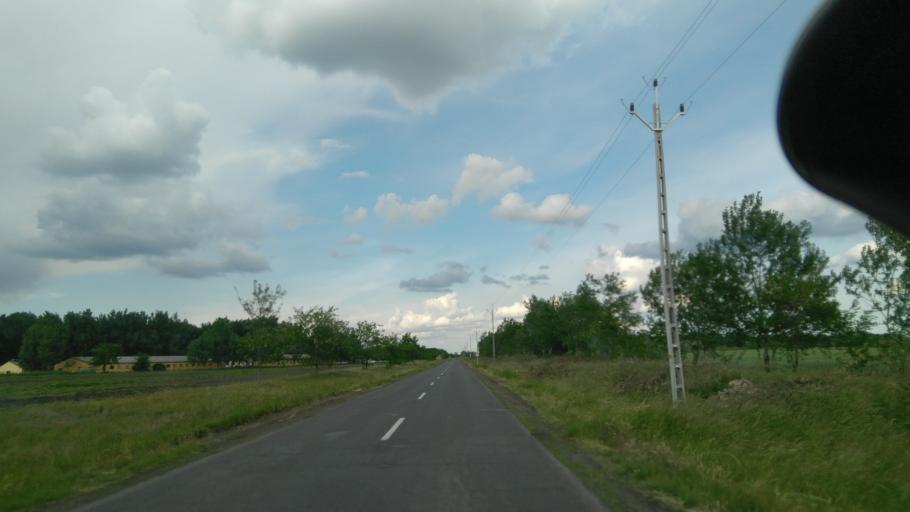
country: HU
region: Bekes
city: Dombegyhaz
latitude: 46.3303
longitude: 21.1000
